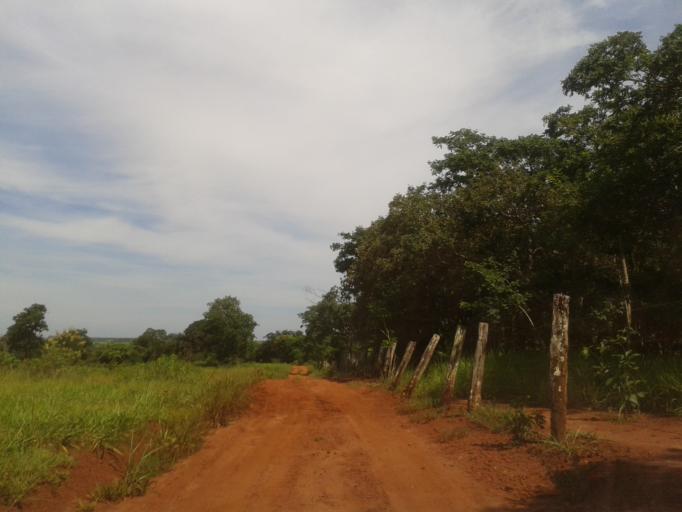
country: BR
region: Minas Gerais
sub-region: Santa Vitoria
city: Santa Vitoria
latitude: -19.1319
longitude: -50.5491
